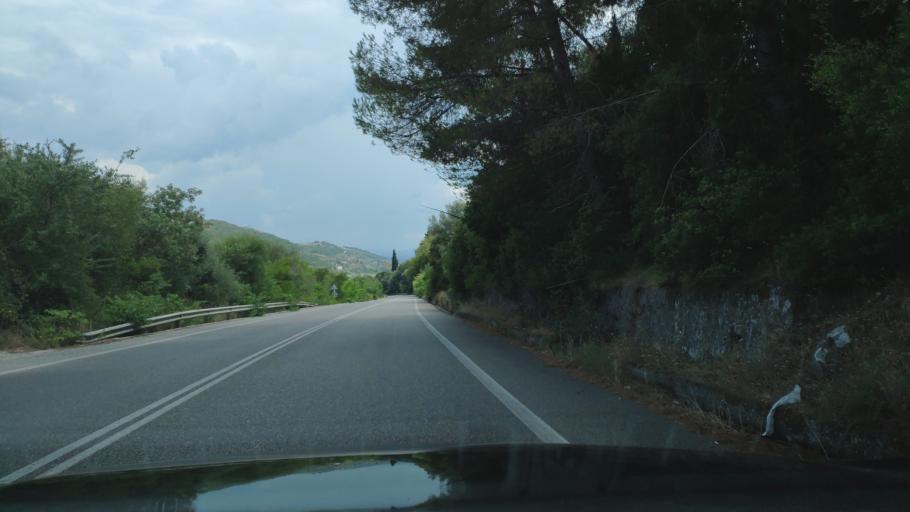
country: GR
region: West Greece
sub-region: Nomos Aitolias kai Akarnanias
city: Krikellos
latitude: 38.9927
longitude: 21.1556
